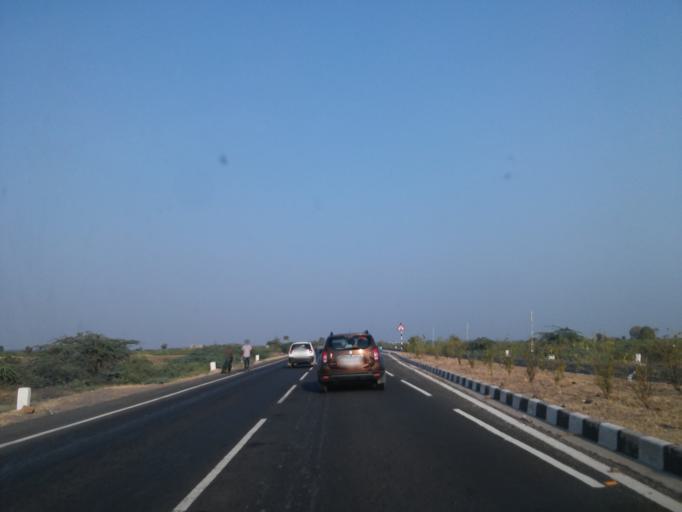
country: IN
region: Gujarat
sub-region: Surendranagar
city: Lakhtar
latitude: 23.0393
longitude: 71.6833
